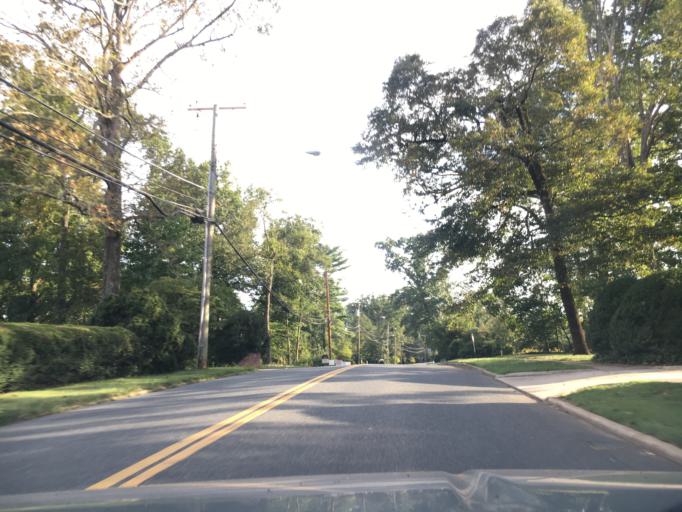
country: US
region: Virginia
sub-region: City of Lynchburg
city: West Lynchburg
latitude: 37.4361
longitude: -79.1965
